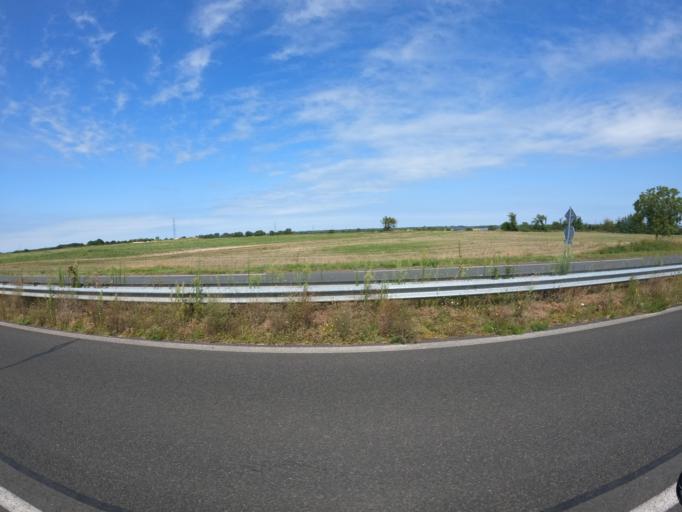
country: FR
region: Poitou-Charentes
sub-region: Departement des Deux-Sevres
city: Frontenay-Rohan-Rohan
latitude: 46.2533
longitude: -0.5489
